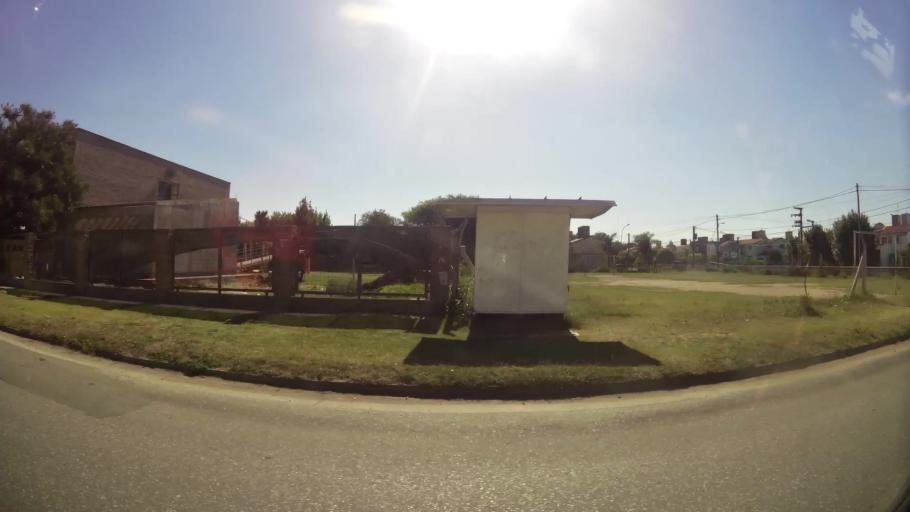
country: AR
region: Cordoba
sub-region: Departamento de Capital
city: Cordoba
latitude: -31.3586
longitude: -64.1839
